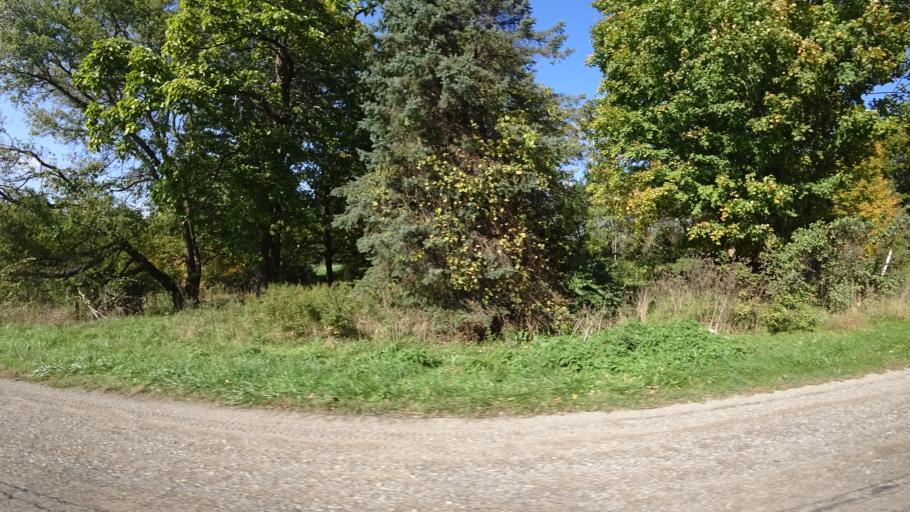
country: US
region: Michigan
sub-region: Jackson County
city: Spring Arbor
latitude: 42.2188
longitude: -84.5120
